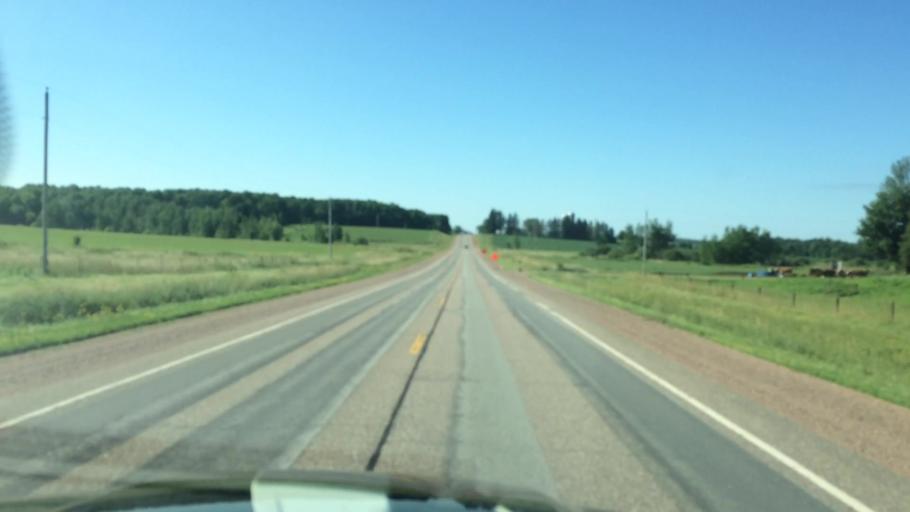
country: US
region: Wisconsin
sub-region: Marathon County
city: Stratford
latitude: 44.9158
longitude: -90.0787
